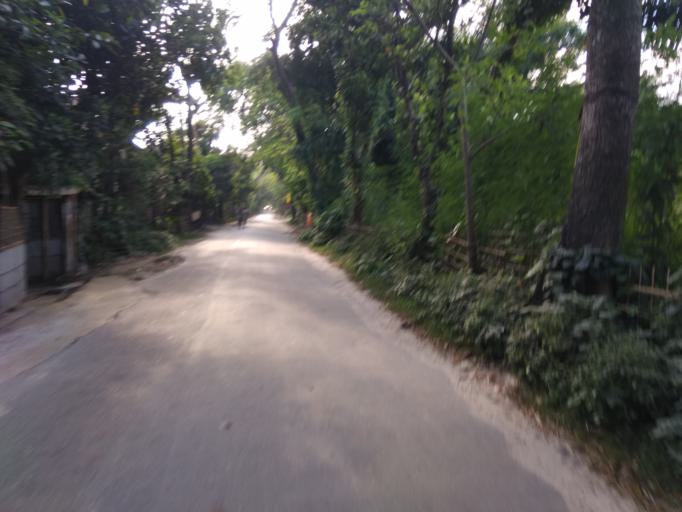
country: BD
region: Rangpur Division
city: Rangpur
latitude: 25.8304
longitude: 89.1186
